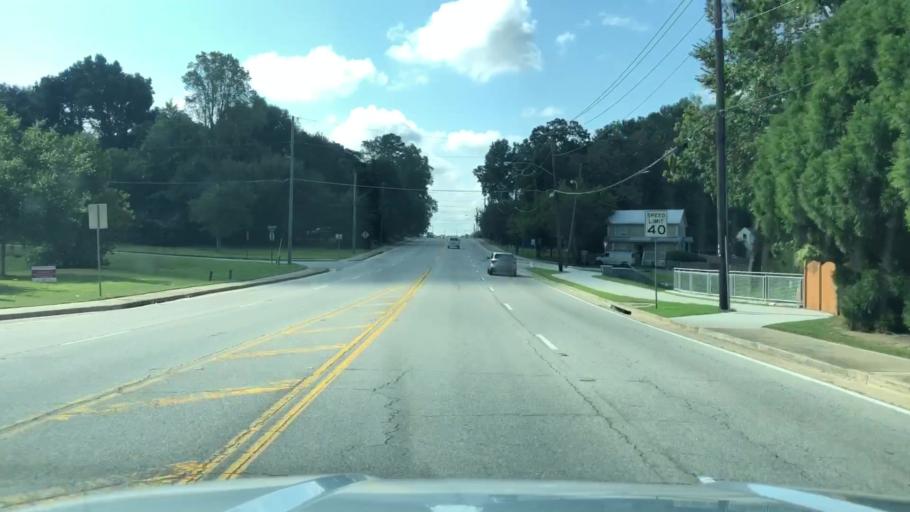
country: US
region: Georgia
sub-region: DeKalb County
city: Chamblee
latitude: 33.8717
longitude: -84.3095
